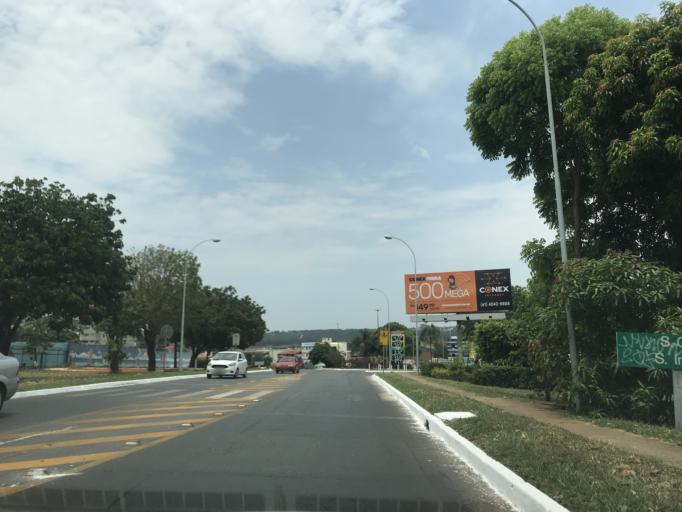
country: BR
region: Federal District
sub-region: Brasilia
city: Brasilia
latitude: -15.6598
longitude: -47.8059
